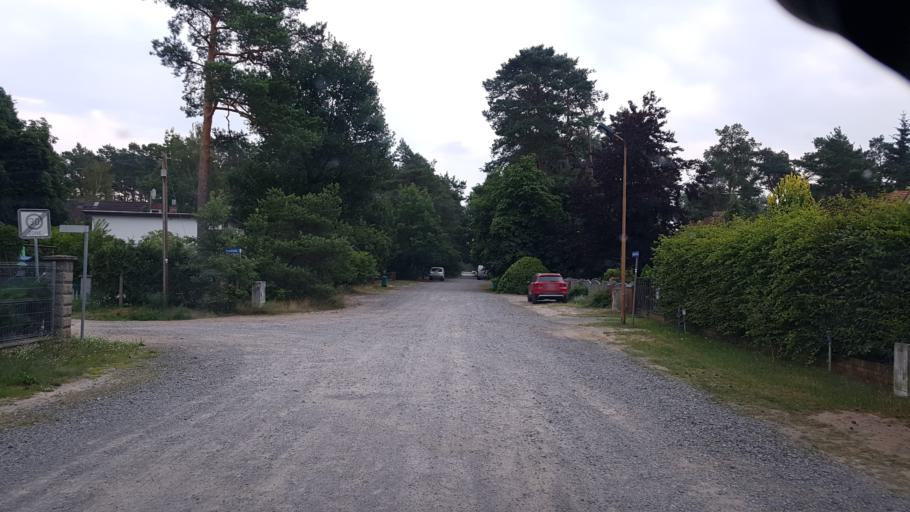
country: DE
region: Brandenburg
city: Gross Koris
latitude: 52.1636
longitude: 13.6954
